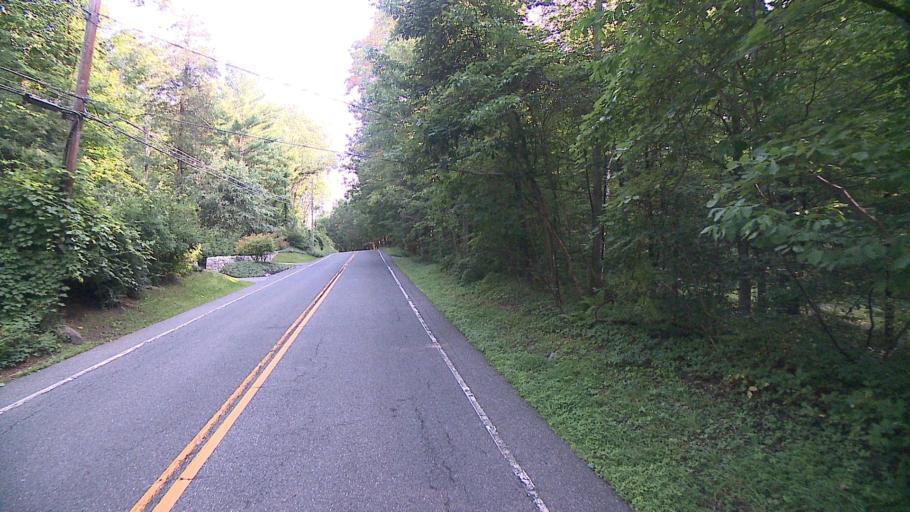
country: US
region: Connecticut
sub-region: Litchfield County
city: Canaan
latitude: 41.8897
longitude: -73.3610
